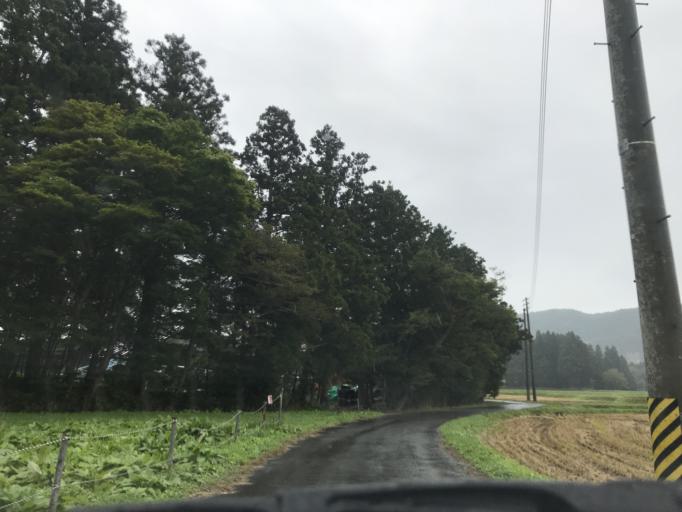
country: JP
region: Iwate
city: Ichinoseki
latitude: 38.9773
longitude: 140.9580
